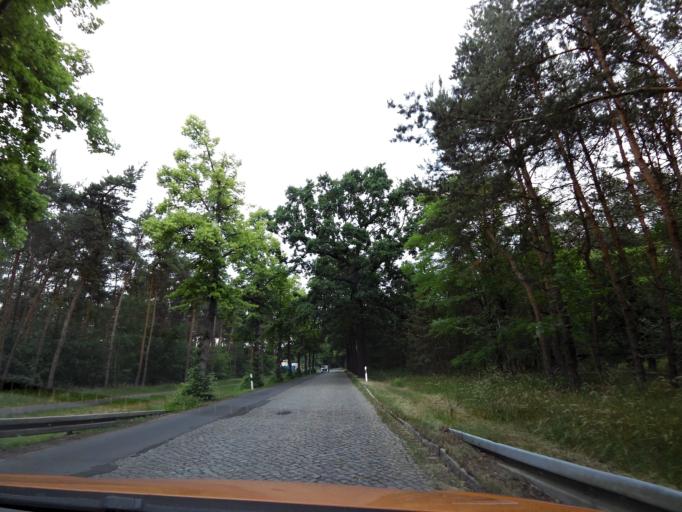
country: DE
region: Brandenburg
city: Rangsdorf
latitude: 52.3150
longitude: 13.3867
